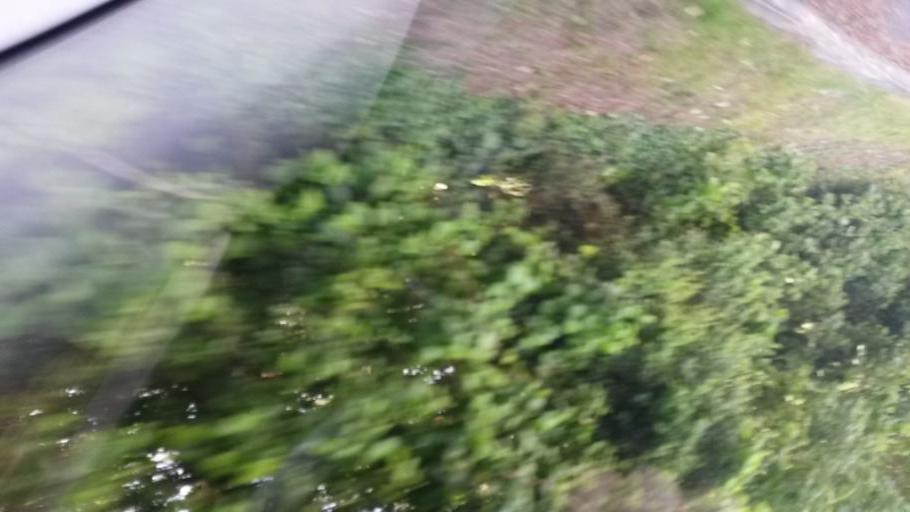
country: IE
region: Leinster
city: Lusk
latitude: 53.5257
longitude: -6.1821
